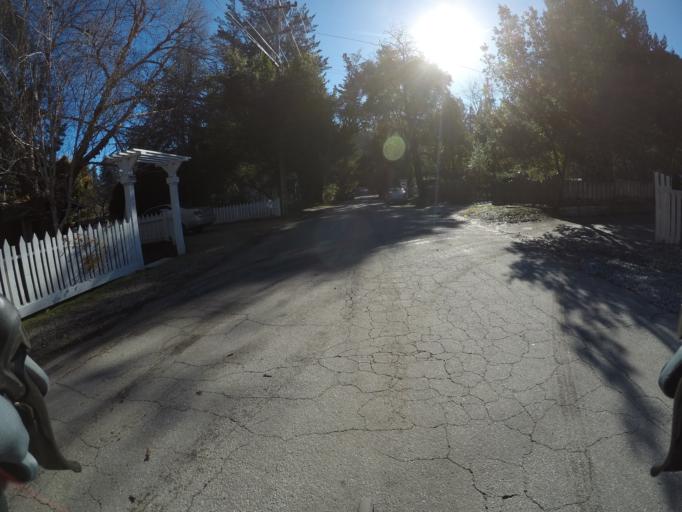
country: US
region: California
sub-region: Santa Cruz County
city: Felton
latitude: 37.0457
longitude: -122.0754
